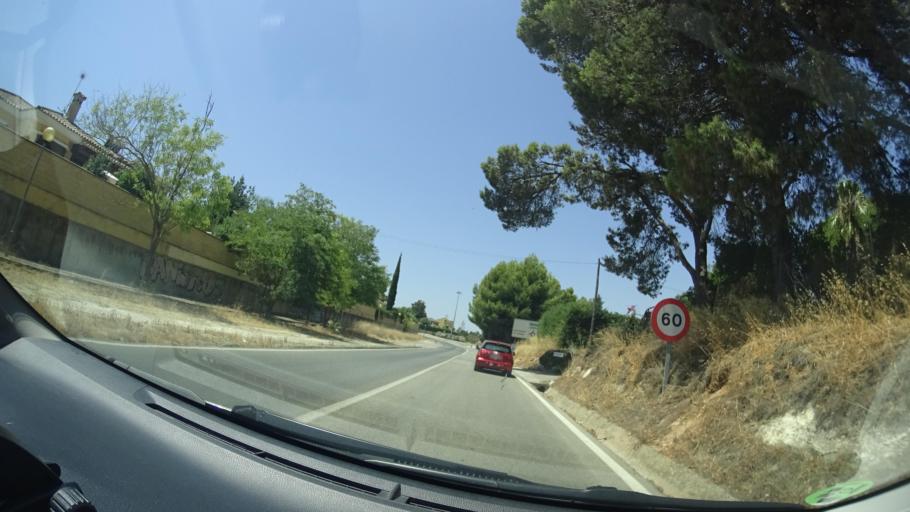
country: ES
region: Andalusia
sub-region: Provincia de Cadiz
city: Jerez de la Frontera
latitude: 36.6656
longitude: -6.1136
